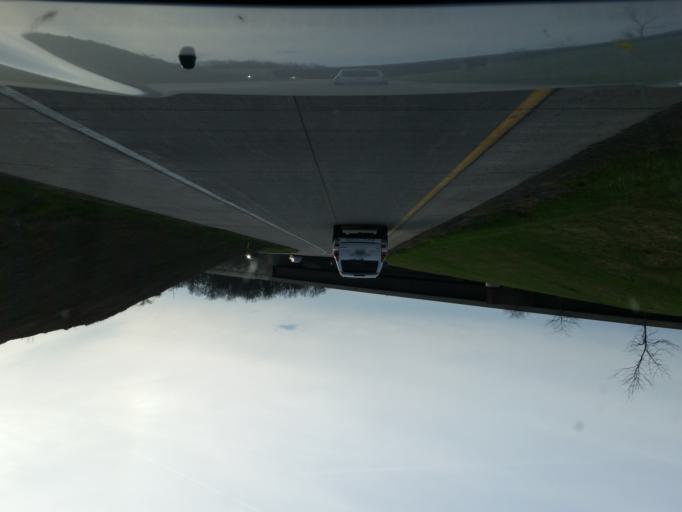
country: US
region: Pennsylvania
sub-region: Centre County
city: Houserville
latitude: 40.8269
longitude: -77.8468
